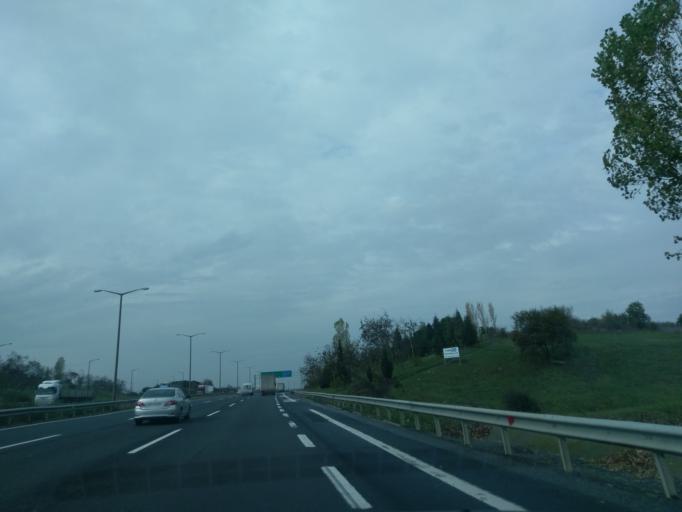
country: TR
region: Istanbul
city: Buyukcavuslu
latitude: 41.1907
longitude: 28.0918
